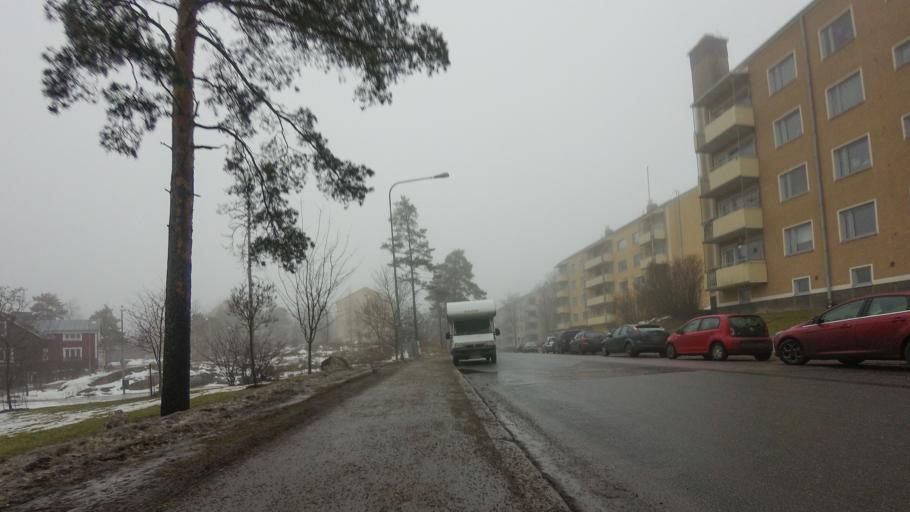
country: FI
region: Uusimaa
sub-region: Helsinki
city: Vantaa
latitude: 60.2029
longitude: 25.0322
